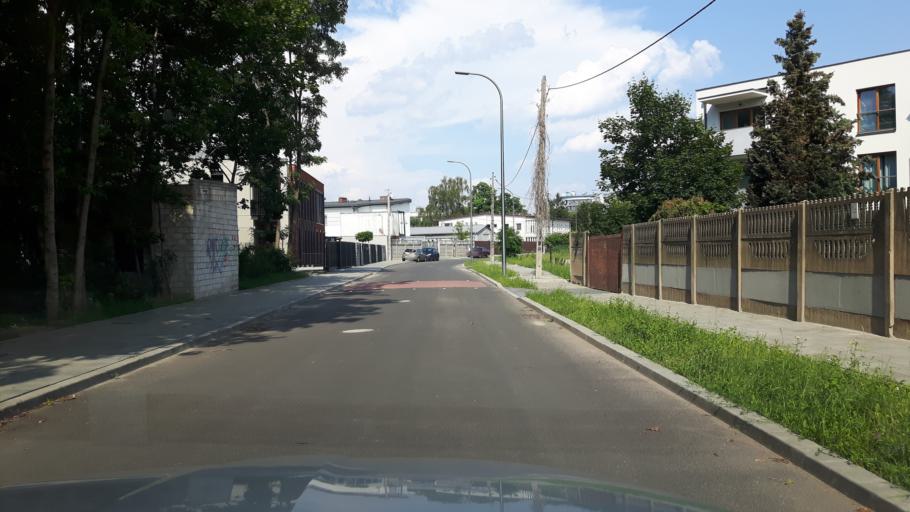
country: PL
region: Masovian Voivodeship
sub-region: Warszawa
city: Targowek
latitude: 52.2751
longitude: 21.0395
